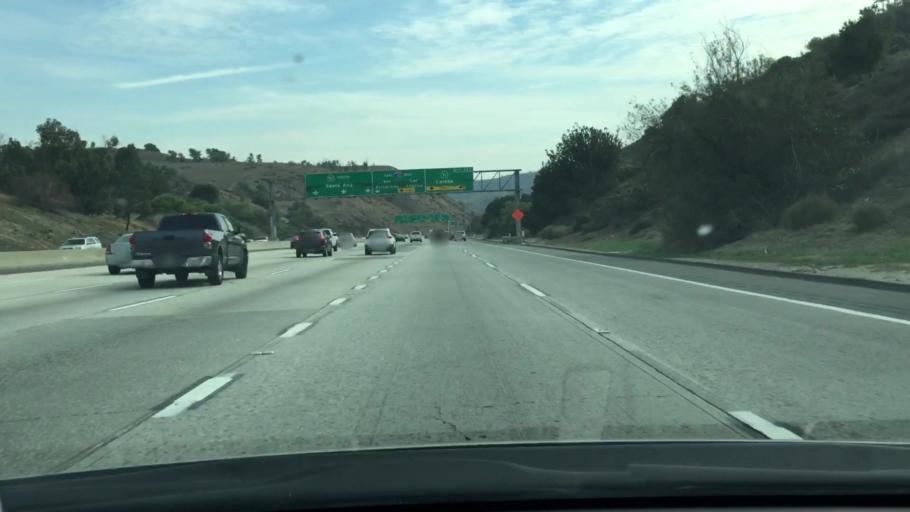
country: US
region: California
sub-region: Los Angeles County
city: San Dimas
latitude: 34.0766
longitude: -117.8131
